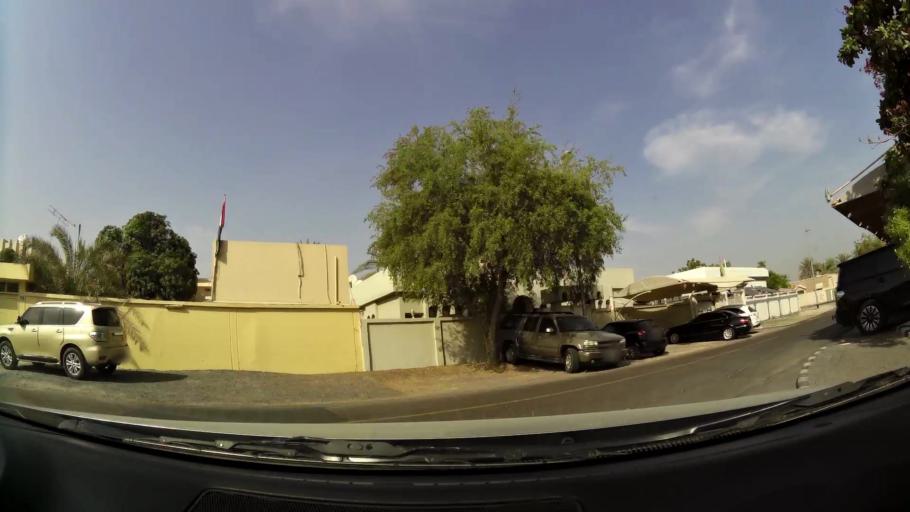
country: AE
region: Ash Shariqah
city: Sharjah
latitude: 25.2189
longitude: 55.3919
